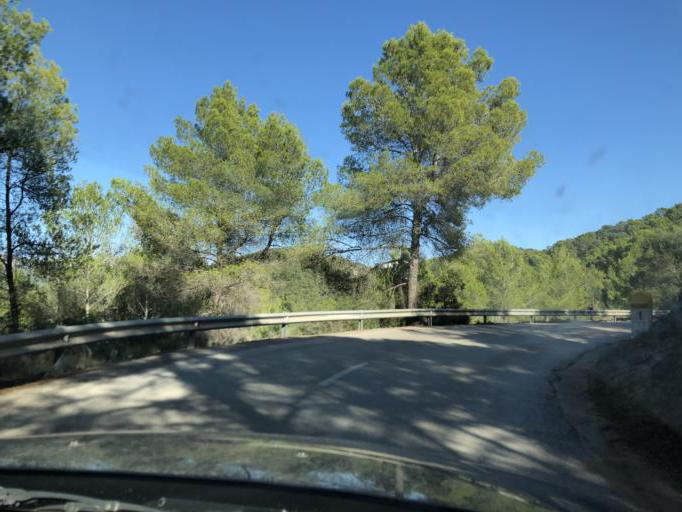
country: ES
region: Balearic Islands
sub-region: Illes Balears
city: Camp de Mar
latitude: 39.5417
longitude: 2.3966
